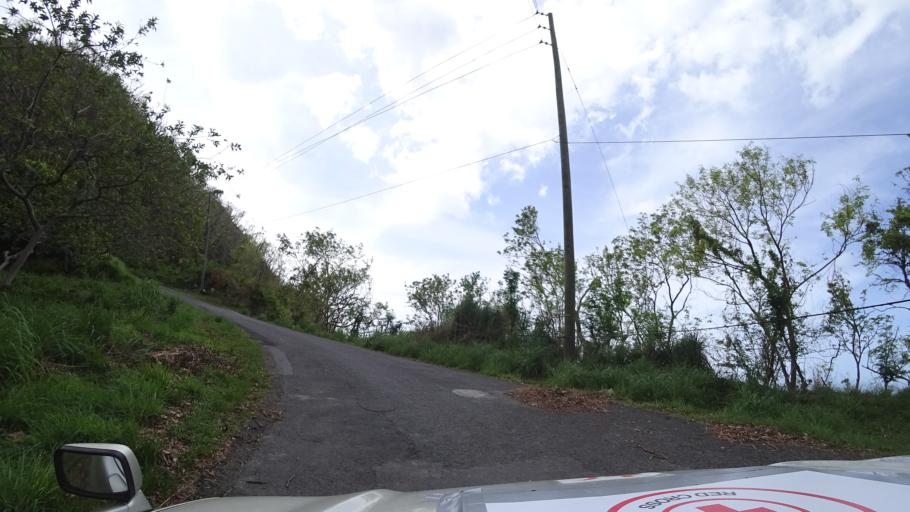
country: DM
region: Saint Luke
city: Pointe Michel
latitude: 15.2468
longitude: -61.3725
